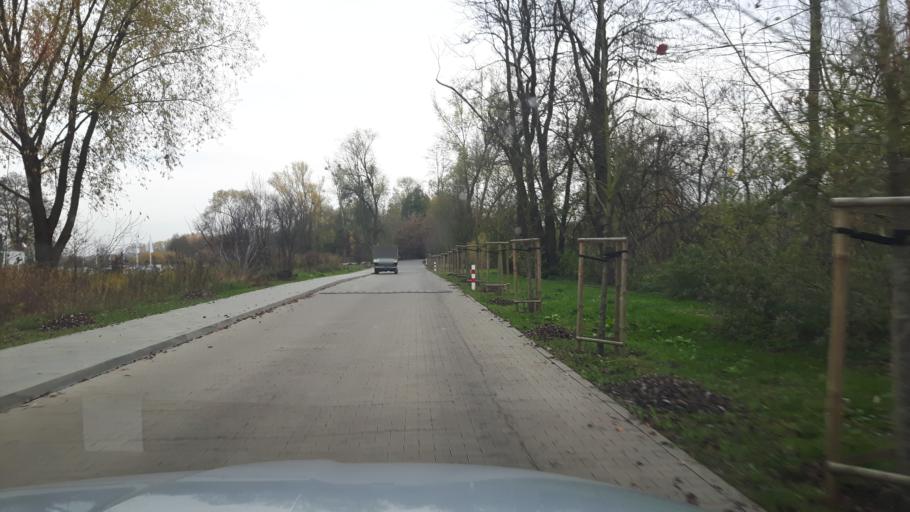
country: PL
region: Masovian Voivodeship
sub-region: Warszawa
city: Ursynow
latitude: 52.1577
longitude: 21.0617
